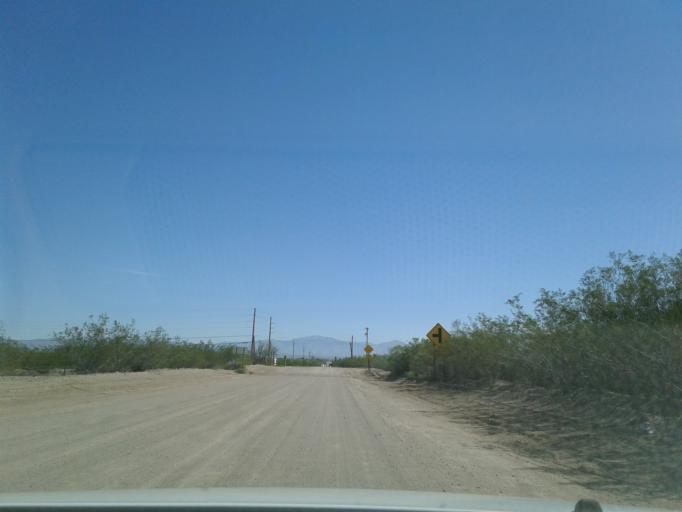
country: US
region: Arizona
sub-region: Pima County
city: Avra Valley
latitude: 32.4293
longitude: -111.3487
